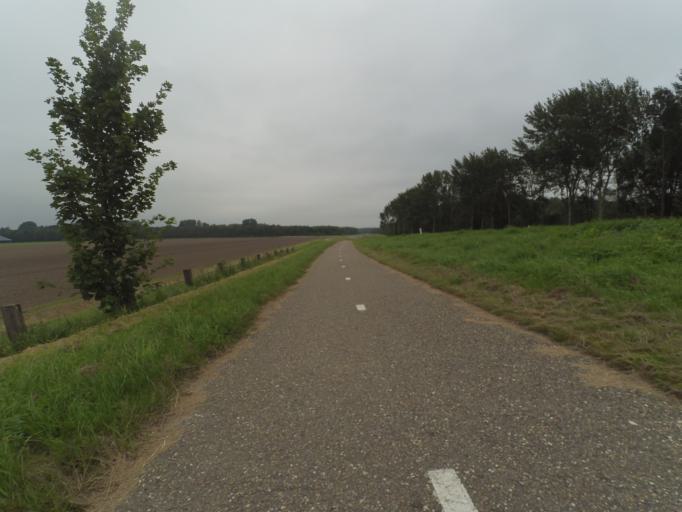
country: NL
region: Flevoland
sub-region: Gemeente Zeewolde
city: Zeewolde
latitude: 52.4109
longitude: 5.4924
